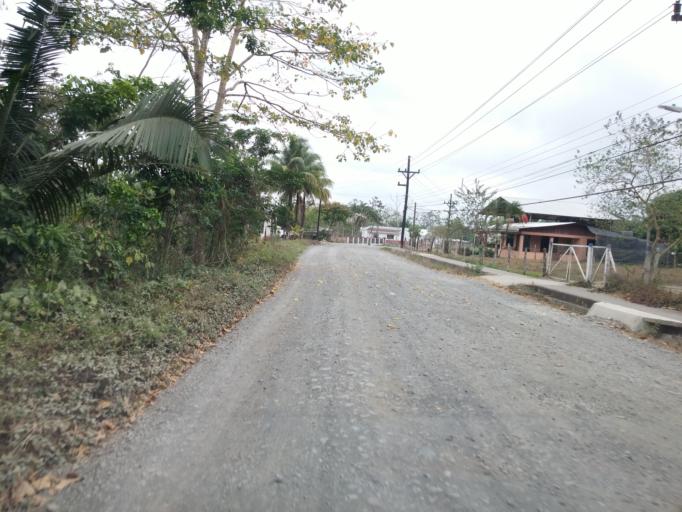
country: CR
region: Alajuela
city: Quesada
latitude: 10.3155
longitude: -84.5221
